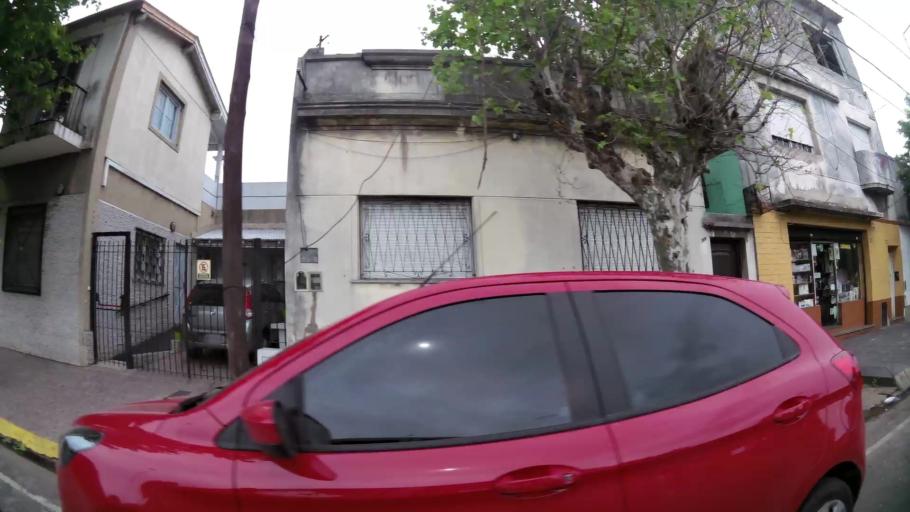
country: AR
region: Buenos Aires
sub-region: Partido de Avellaneda
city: Avellaneda
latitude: -34.6584
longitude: -58.3592
